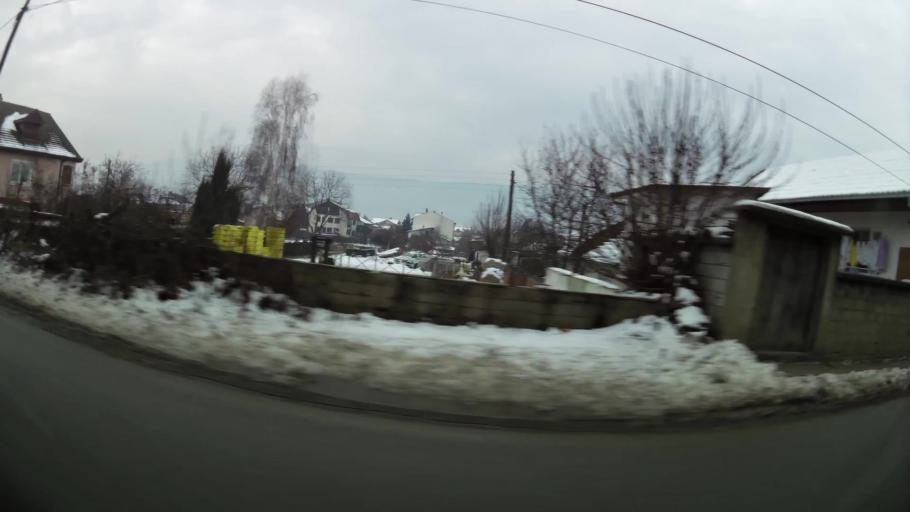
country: MK
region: Saraj
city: Saraj
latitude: 42.0102
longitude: 21.3313
